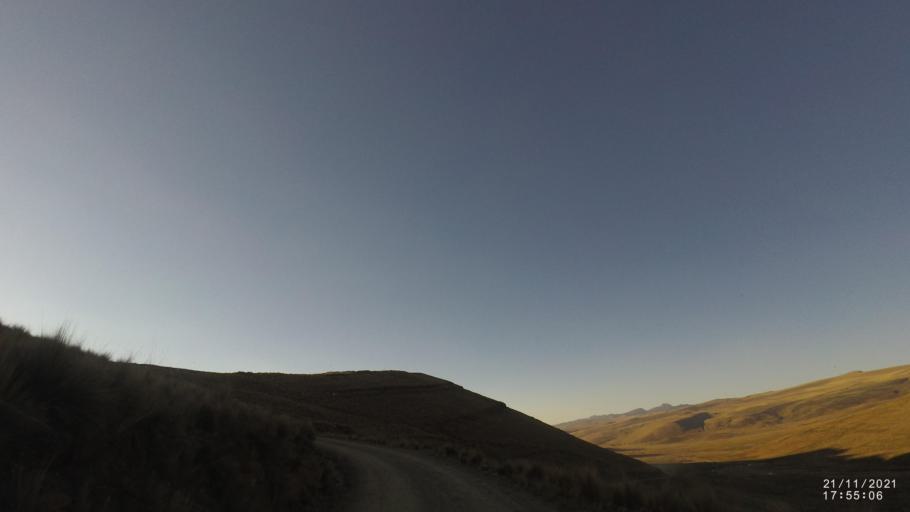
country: BO
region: Cochabamba
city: Cochabamba
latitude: -17.2215
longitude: -66.2361
